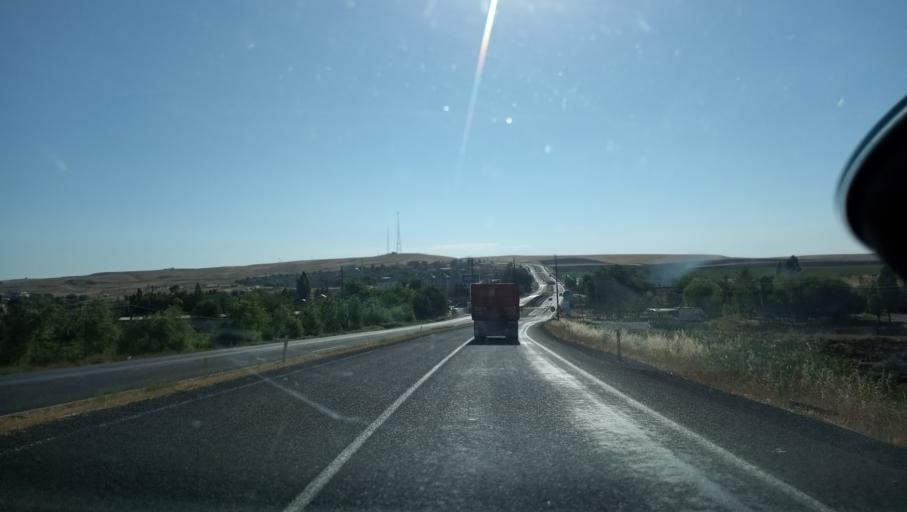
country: TR
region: Diyarbakir
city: Sur
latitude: 37.9907
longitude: 40.3791
